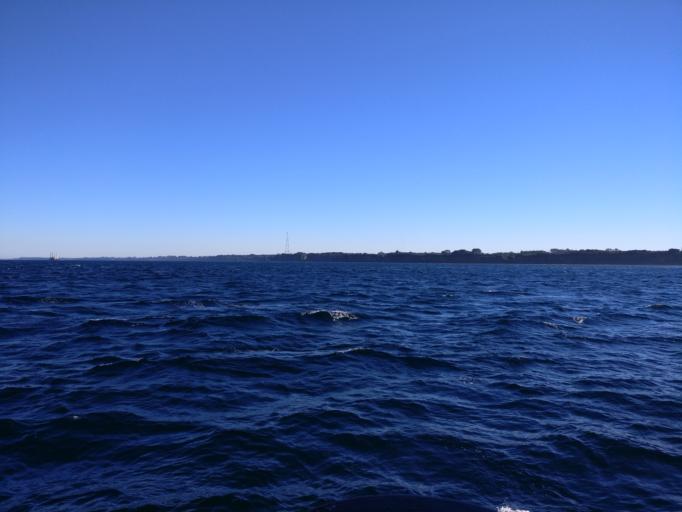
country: CL
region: Los Lagos
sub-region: Provincia de Chiloe
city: Ancud
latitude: -41.8113
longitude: -73.4826
